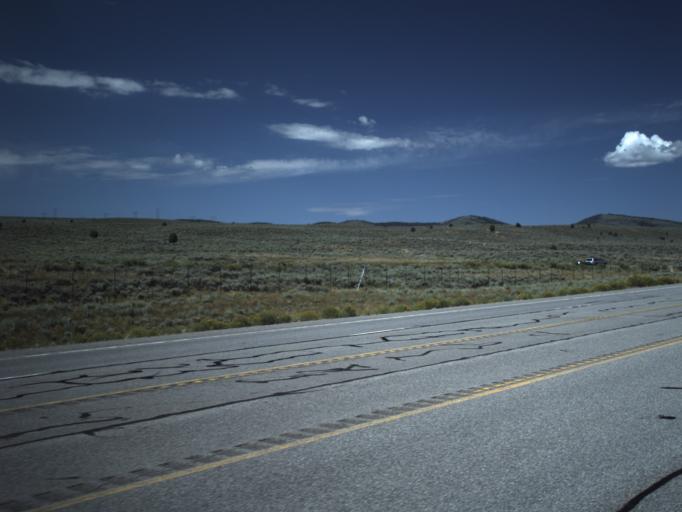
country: US
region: Utah
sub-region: Carbon County
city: Helper
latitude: 39.8389
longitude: -110.9837
